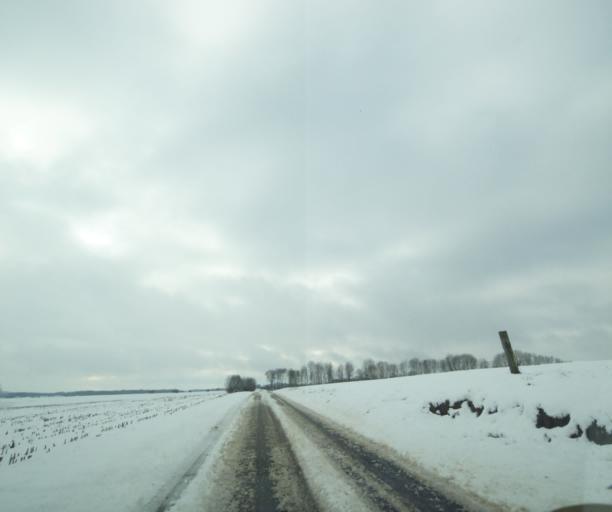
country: FR
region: Champagne-Ardenne
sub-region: Departement de la Haute-Marne
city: Montier-en-Der
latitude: 48.5057
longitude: 4.6871
